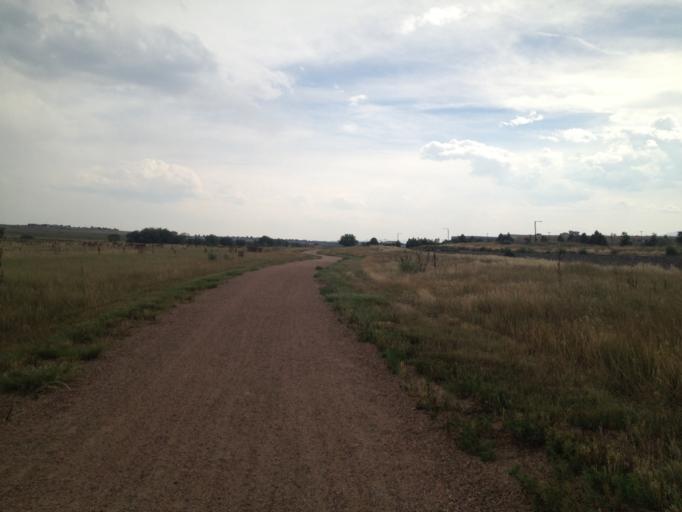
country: US
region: Colorado
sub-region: Boulder County
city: Lafayette
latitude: 39.9716
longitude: -105.0810
